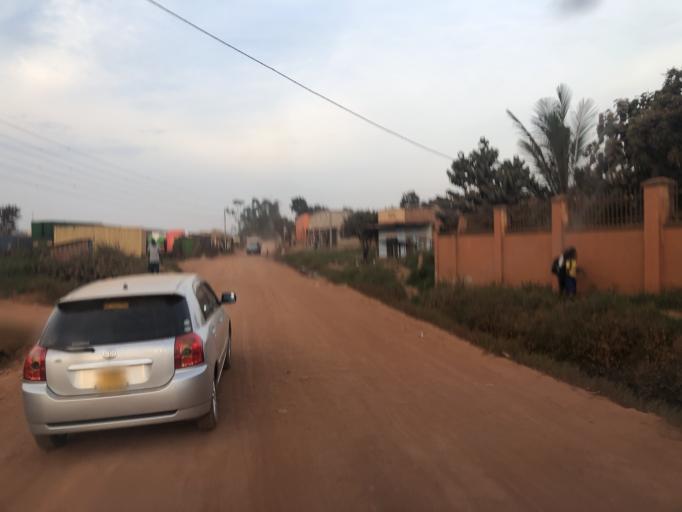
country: UG
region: Central Region
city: Kampala Central Division
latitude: 0.3000
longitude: 32.5133
